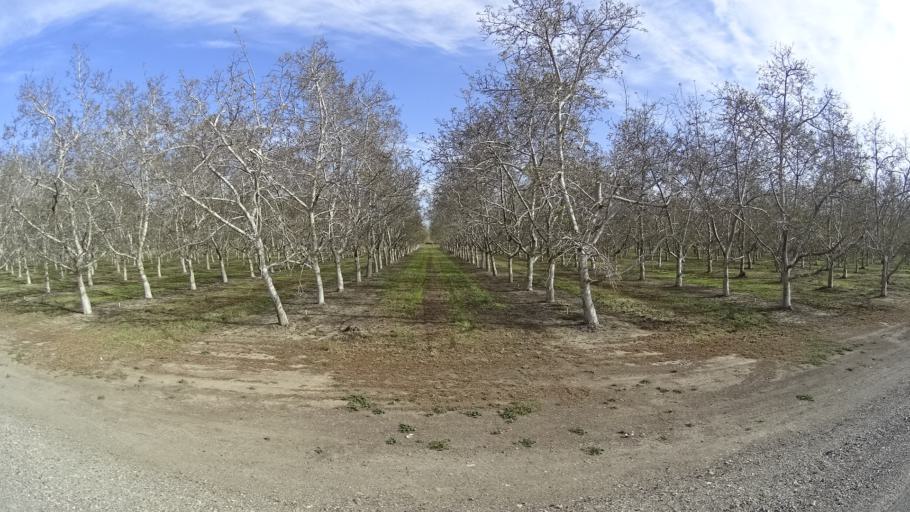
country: US
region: California
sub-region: Glenn County
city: Hamilton City
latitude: 39.6306
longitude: -122.0255
